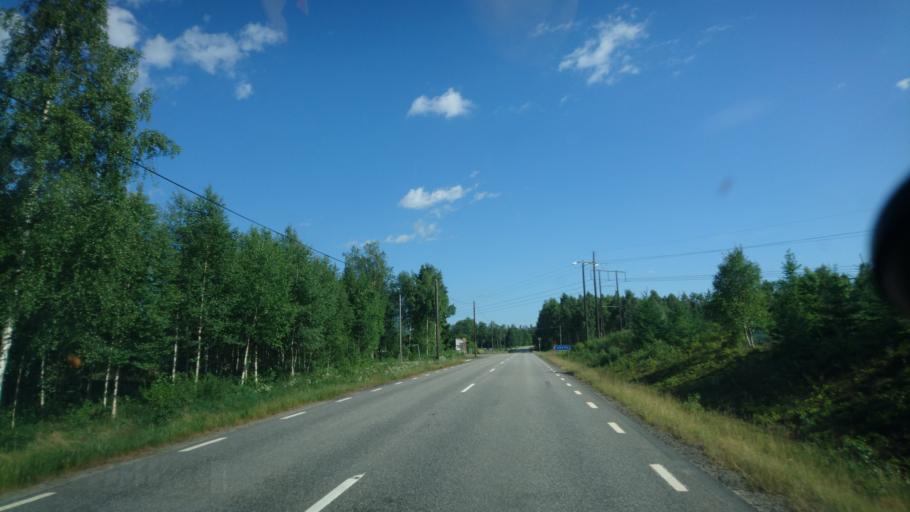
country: SE
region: Skane
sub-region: Osby Kommun
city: Lonsboda
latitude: 56.4686
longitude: 14.2278
